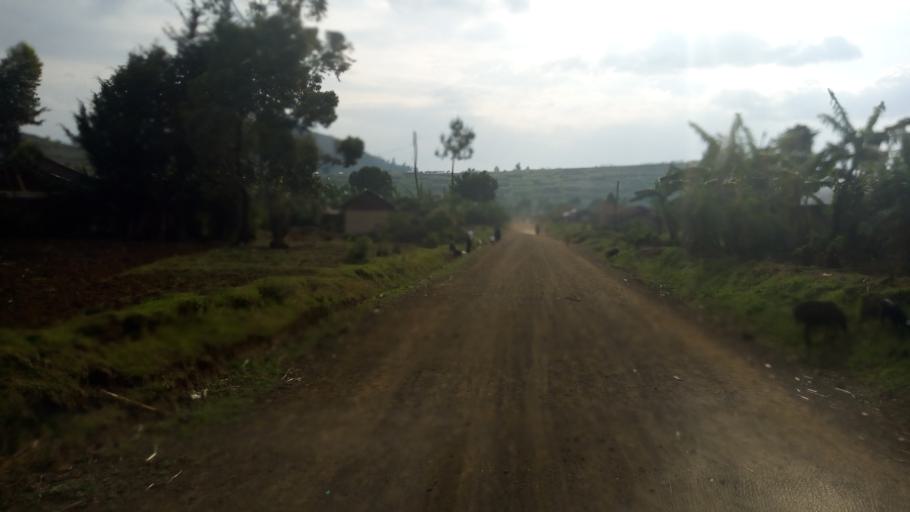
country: UG
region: Western Region
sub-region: Kisoro District
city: Kisoro
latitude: -1.3027
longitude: 29.7075
